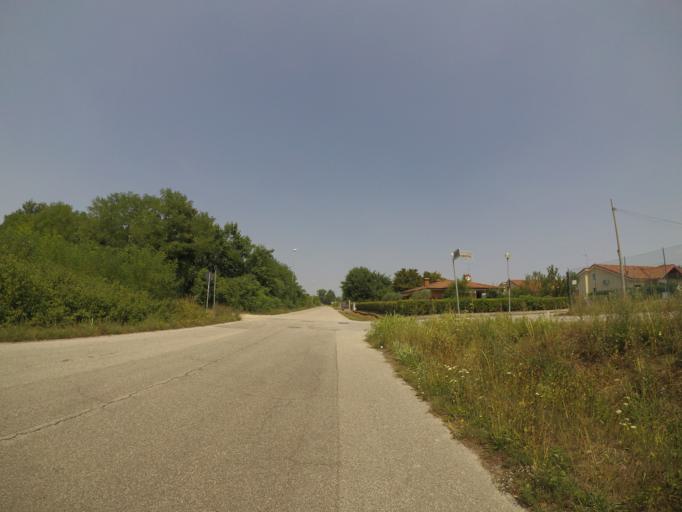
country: IT
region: Friuli Venezia Giulia
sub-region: Provincia di Udine
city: Basiliano-Vissandone
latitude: 46.0217
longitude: 13.1014
